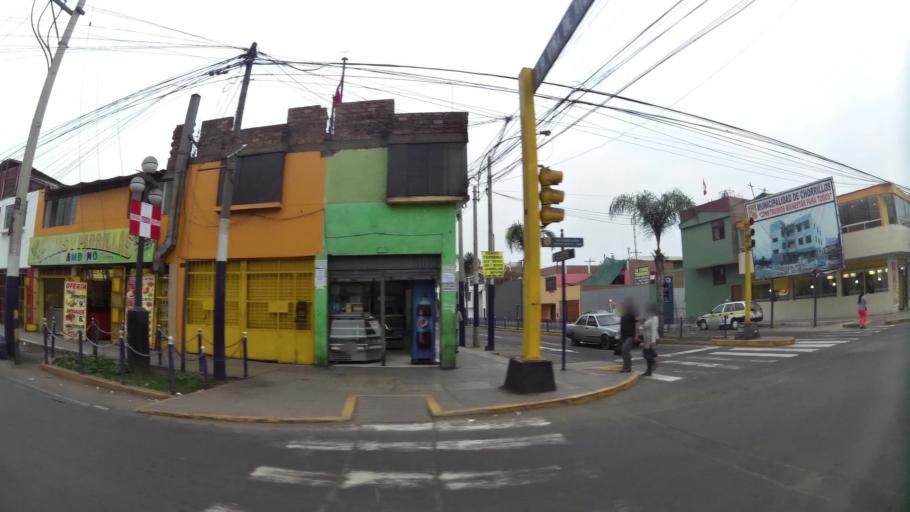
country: PE
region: Lima
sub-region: Lima
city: Surco
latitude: -12.1892
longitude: -77.0142
